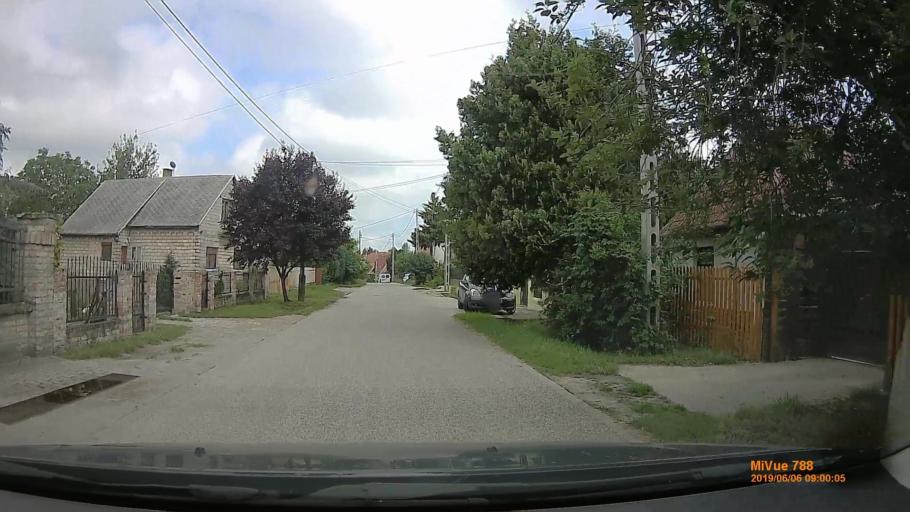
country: HU
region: Pest
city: Maglod
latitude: 47.4483
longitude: 19.3454
